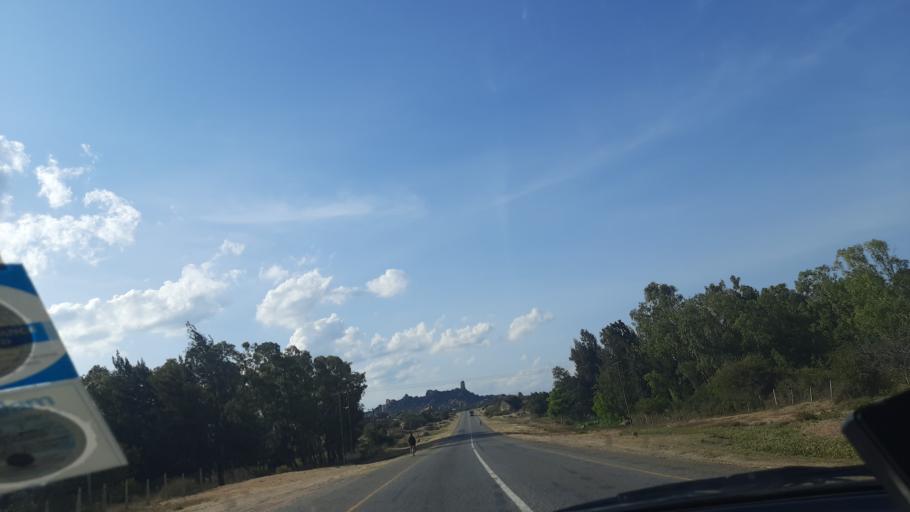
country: TZ
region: Singida
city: Puma
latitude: -4.9842
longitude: 34.7559
